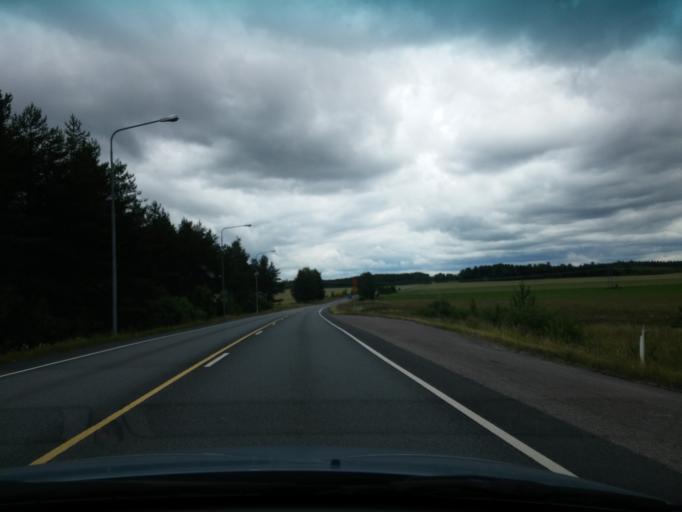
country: FI
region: Uusimaa
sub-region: Porvoo
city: Porvoo
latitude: 60.3935
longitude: 25.6064
